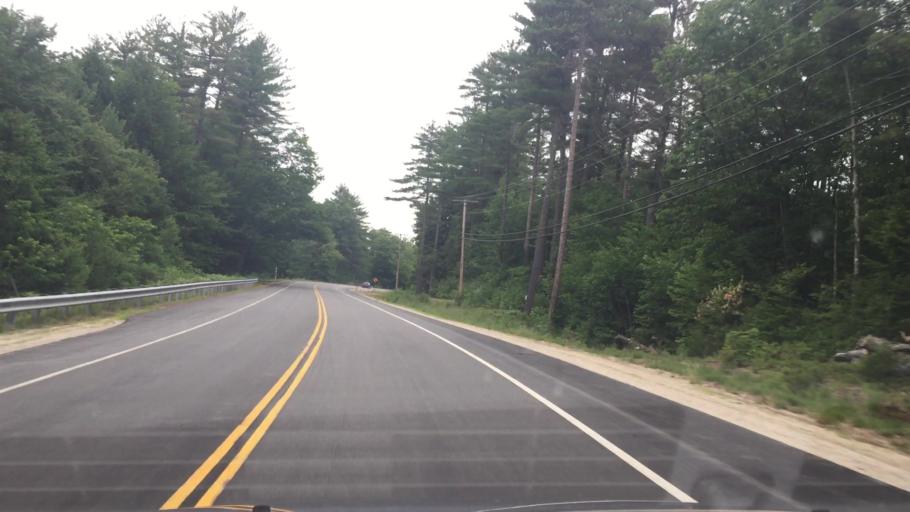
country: US
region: New Hampshire
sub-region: Carroll County
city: Tamworth
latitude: 43.8420
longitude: -71.2649
